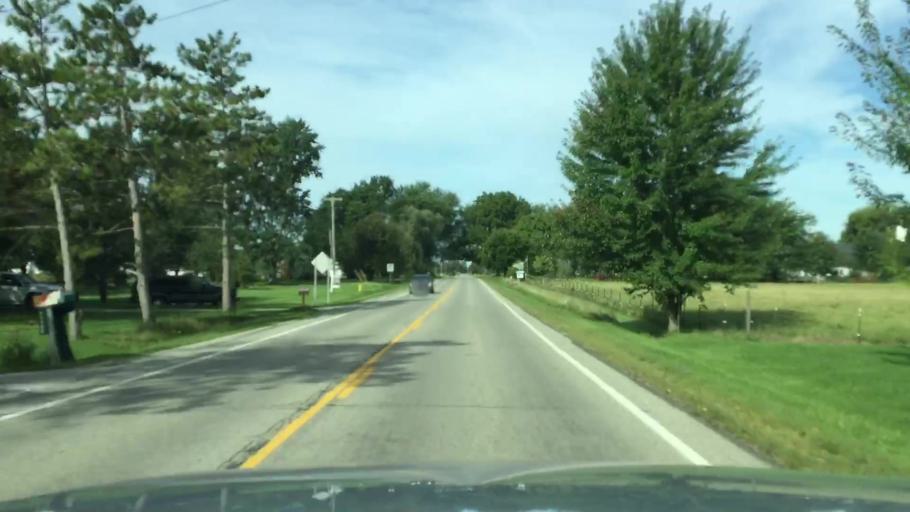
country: US
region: Michigan
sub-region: Genesee County
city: Montrose
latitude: 43.1179
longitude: -83.8977
